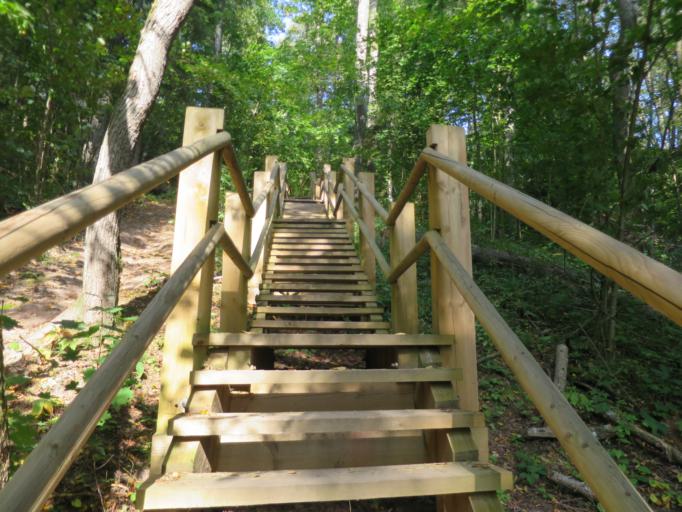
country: LV
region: Sigulda
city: Sigulda
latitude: 57.1510
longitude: 24.8118
